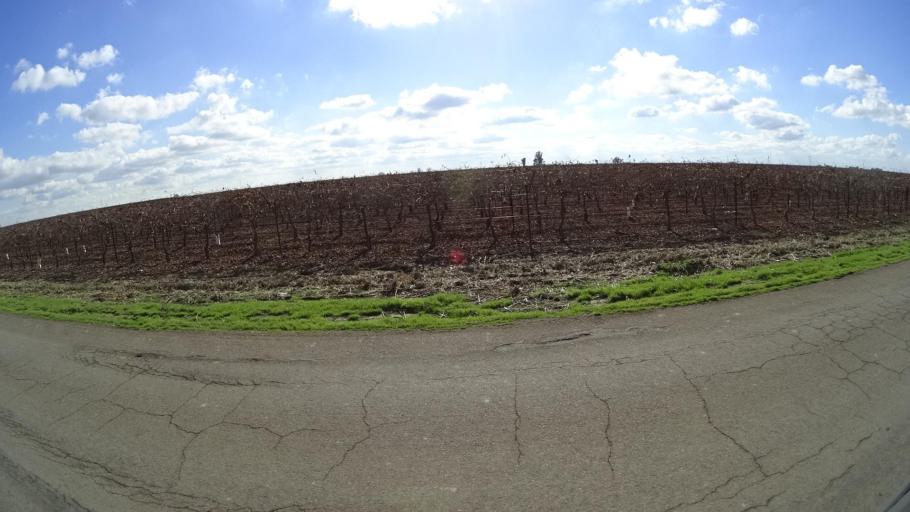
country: US
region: California
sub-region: Kern County
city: Delano
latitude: 35.7323
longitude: -119.2910
